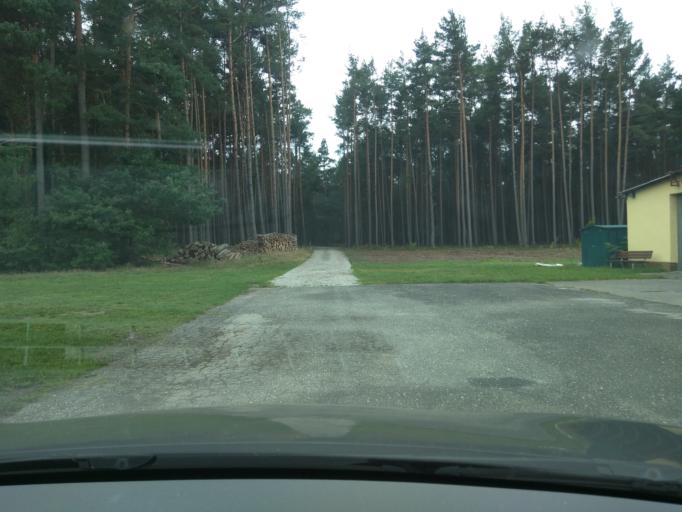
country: DE
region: Bavaria
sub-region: Upper Palatinate
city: Wackersdorf
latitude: 49.3394
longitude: 12.1851
